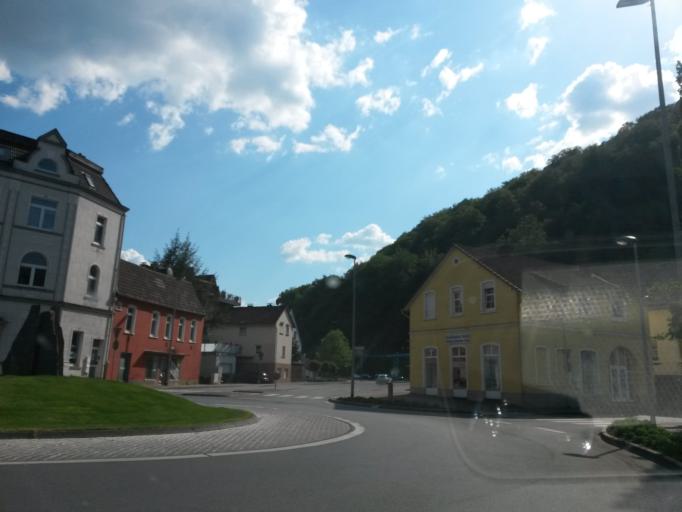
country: DE
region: North Rhine-Westphalia
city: Plettenberg
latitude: 51.2156
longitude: 7.8728
